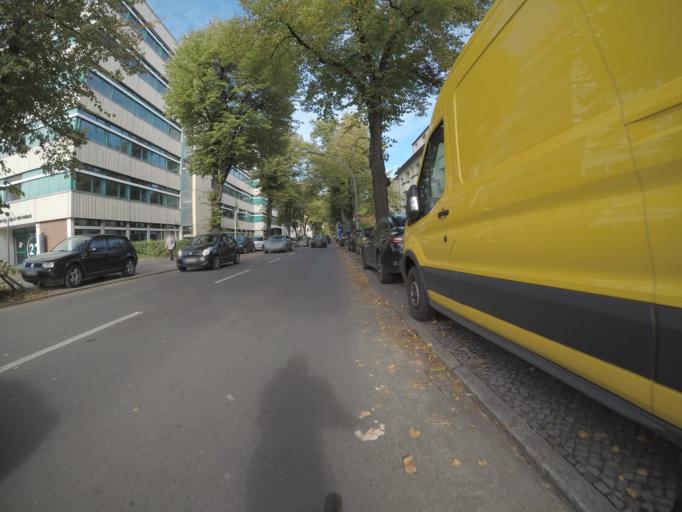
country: DE
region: Berlin
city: Mariendorf
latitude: 52.4456
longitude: 13.3795
